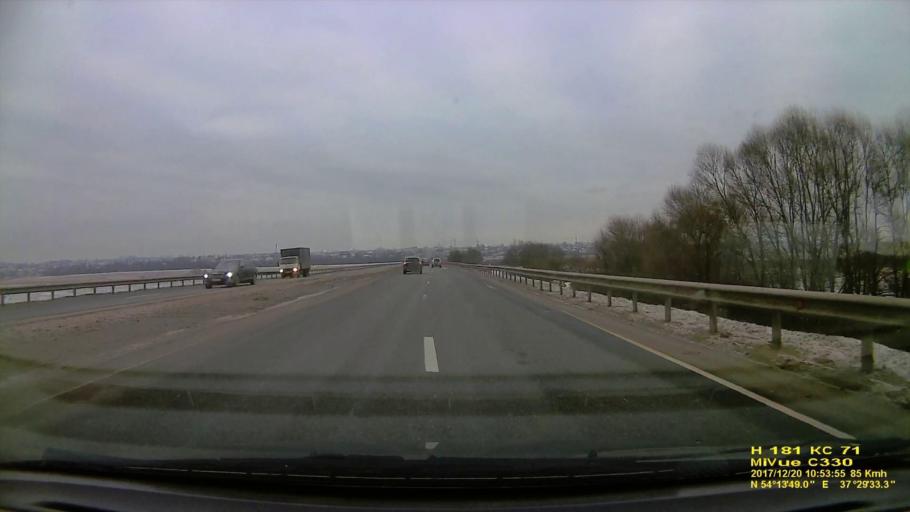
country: RU
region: Tula
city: Barsuki
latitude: 54.2304
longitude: 37.4929
